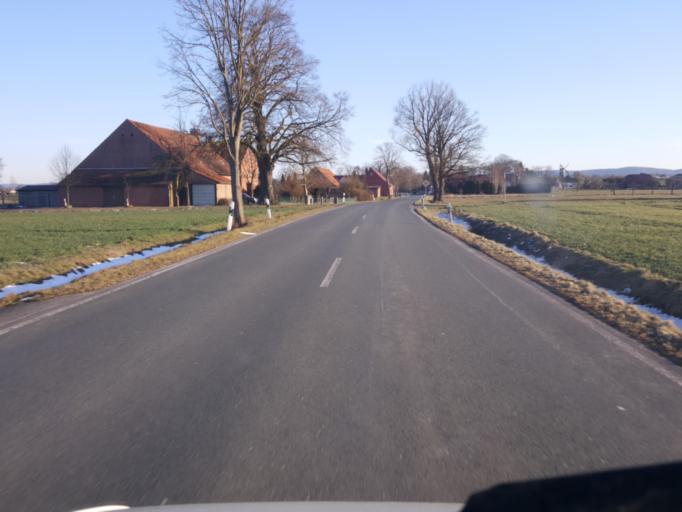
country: DE
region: North Rhine-Westphalia
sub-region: Regierungsbezirk Detmold
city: Hille
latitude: 52.3592
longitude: 8.7298
